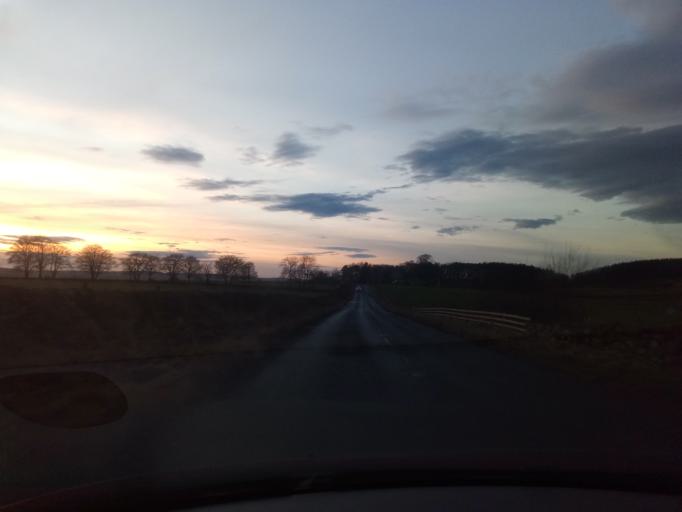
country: GB
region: England
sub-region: Northumberland
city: Otterburn
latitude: 55.2318
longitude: -2.1379
